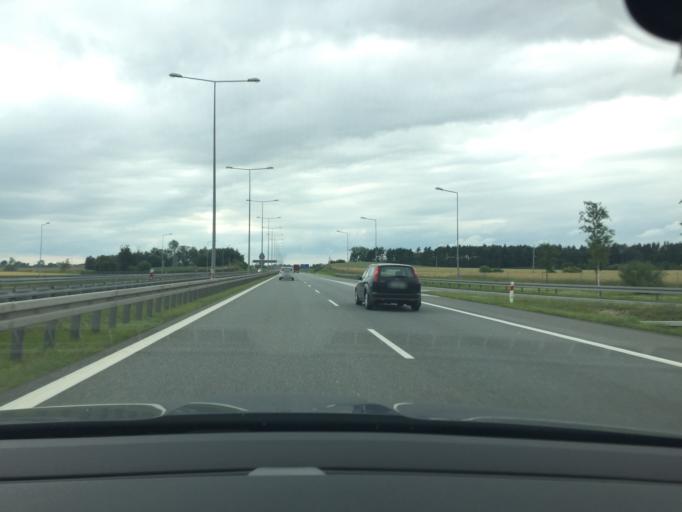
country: PL
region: Greater Poland Voivodeship
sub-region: Powiat poznanski
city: Buk
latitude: 52.3775
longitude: 16.5635
